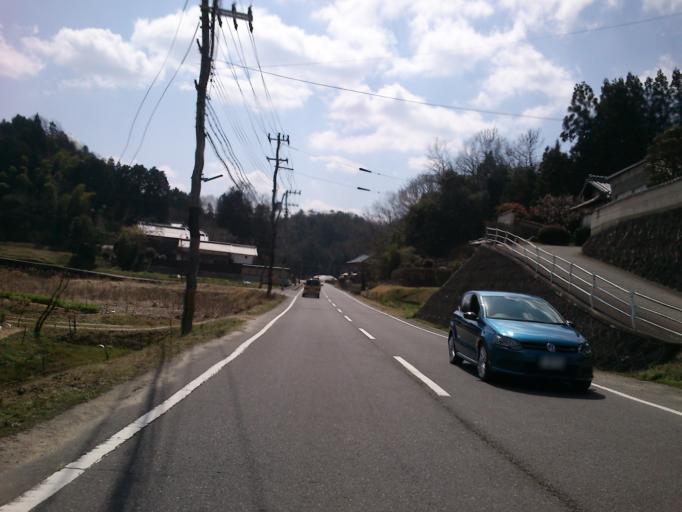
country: JP
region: Mie
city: Ueno-ebisumachi
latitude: 34.7322
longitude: 136.0206
